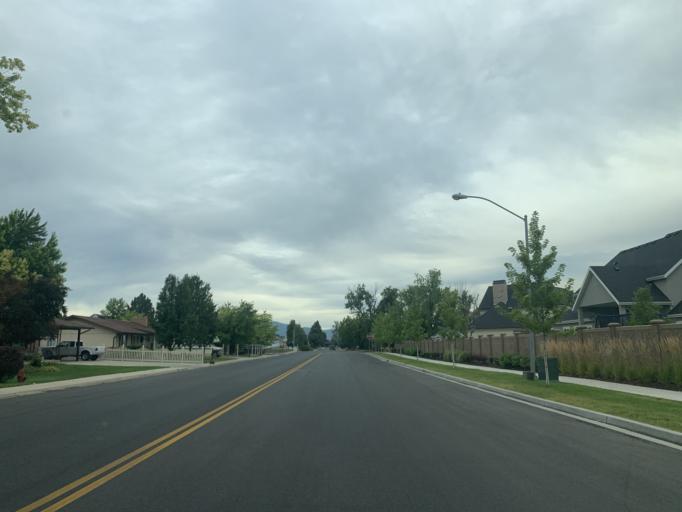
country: US
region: Utah
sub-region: Utah County
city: Orem
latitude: 40.2582
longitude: -111.6949
